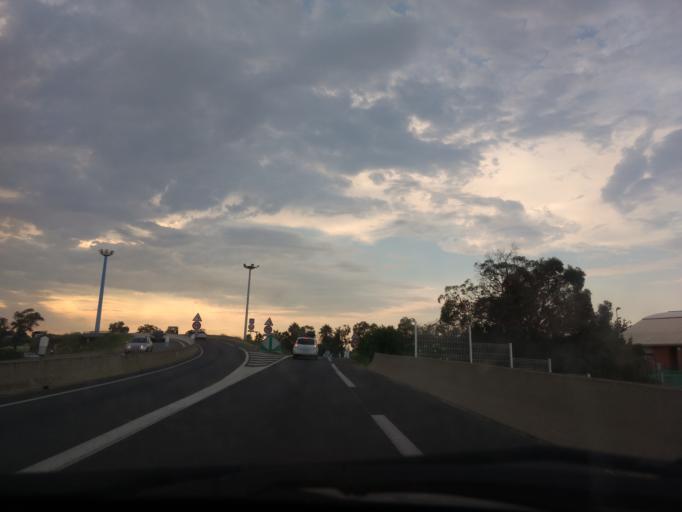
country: FR
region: Languedoc-Roussillon
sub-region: Departement des Pyrenees-Orientales
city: Canet-en-Roussillon
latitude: 42.7018
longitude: 3.0175
